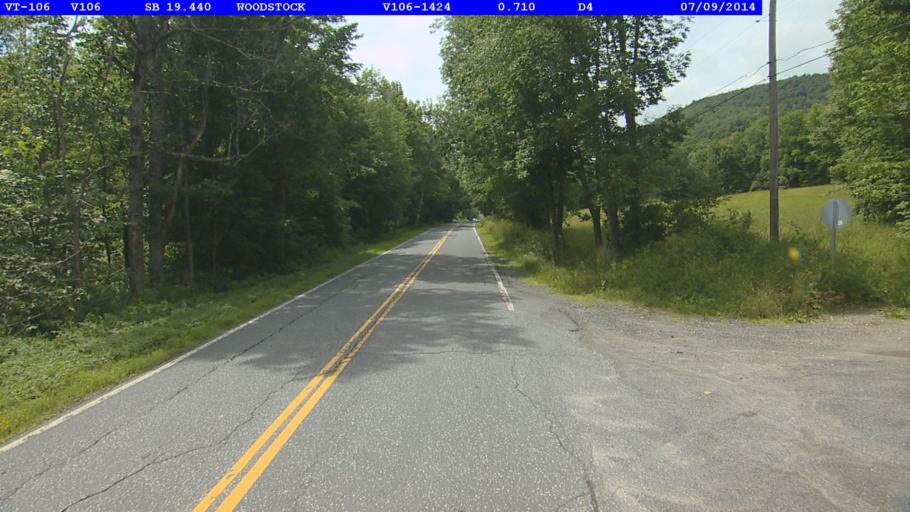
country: US
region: Vermont
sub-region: Windsor County
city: Woodstock
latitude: 43.5489
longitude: -72.5517
